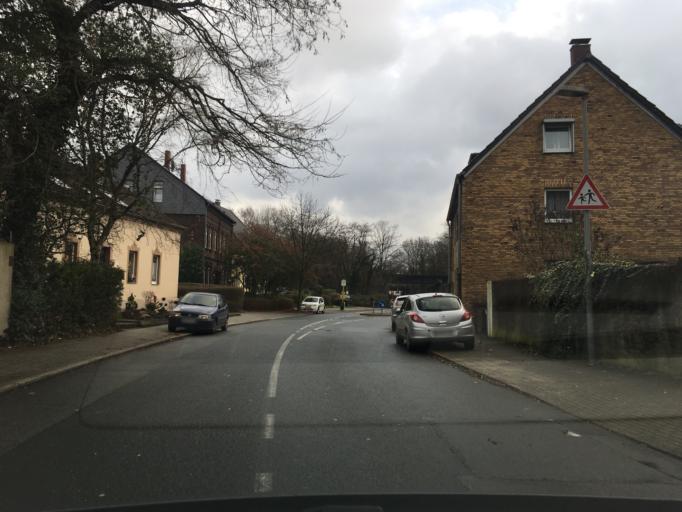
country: DE
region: North Rhine-Westphalia
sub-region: Regierungsbezirk Dusseldorf
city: Oberhausen
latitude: 51.4593
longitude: 6.8330
